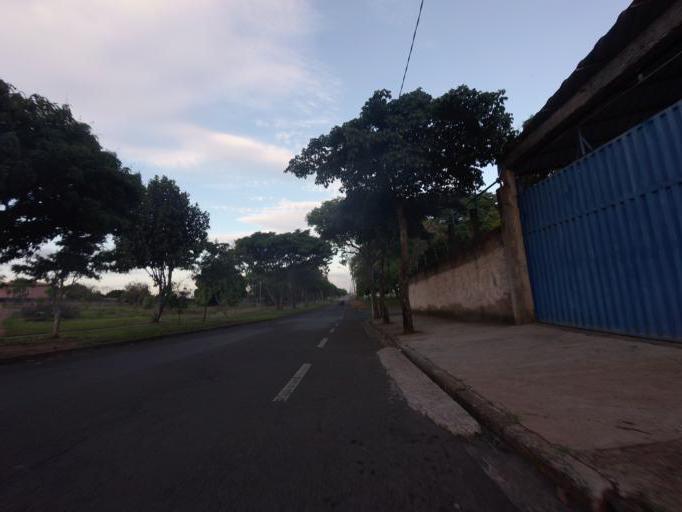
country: BR
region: Sao Paulo
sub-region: Piracicaba
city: Piracicaba
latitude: -22.7636
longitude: -47.5912
